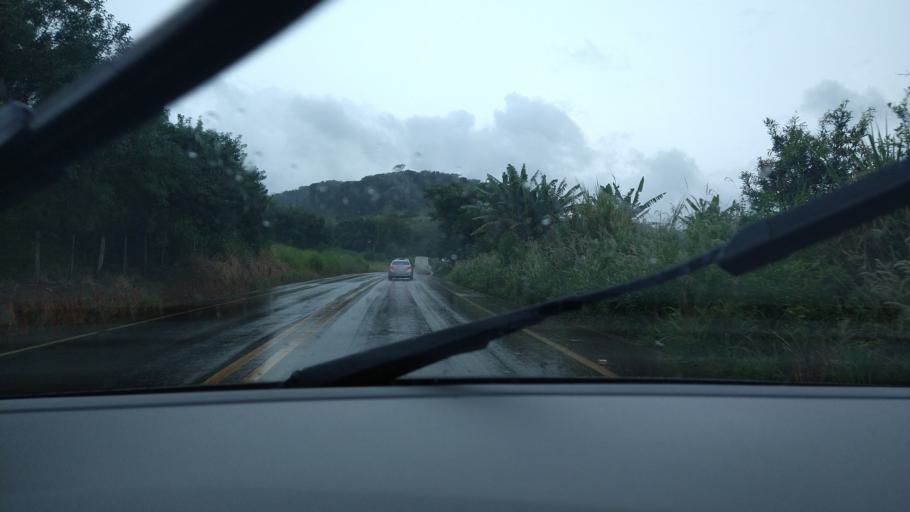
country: BR
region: Minas Gerais
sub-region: Vicosa
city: Vicosa
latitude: -20.6280
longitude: -42.8701
